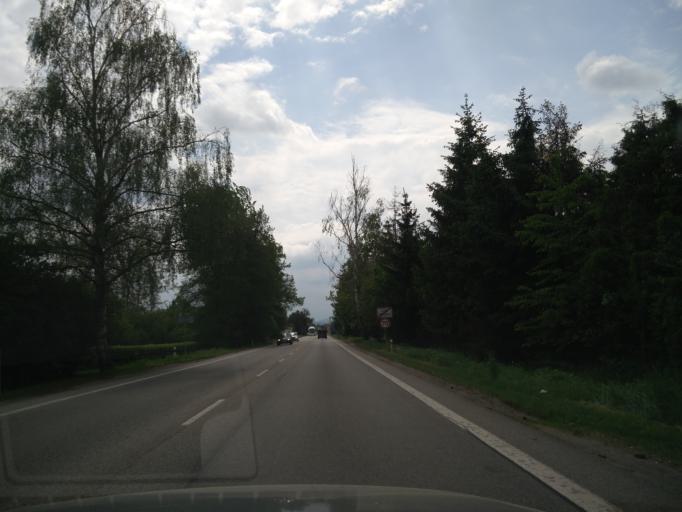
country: CZ
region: Jihocesky
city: Litvinovice
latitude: 48.9662
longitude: 14.4619
